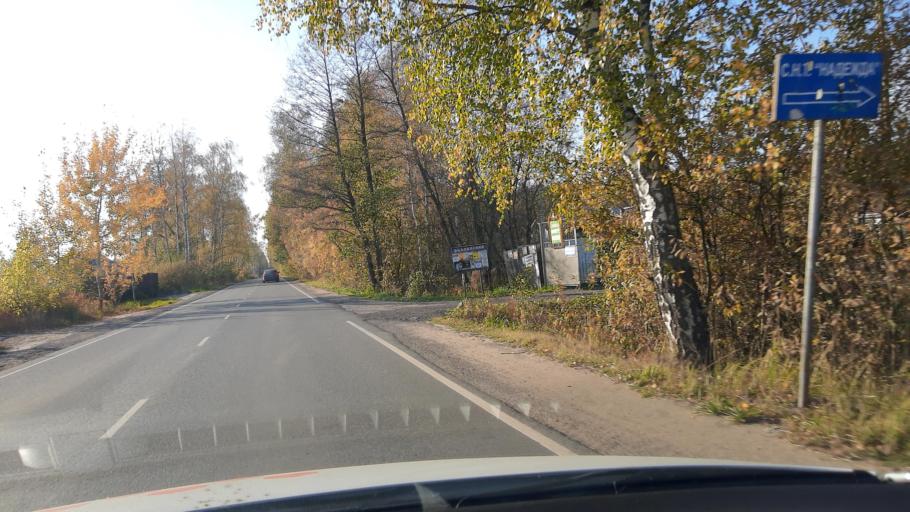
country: RU
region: Moskovskaya
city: Elektrostal'
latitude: 55.8005
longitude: 38.3828
